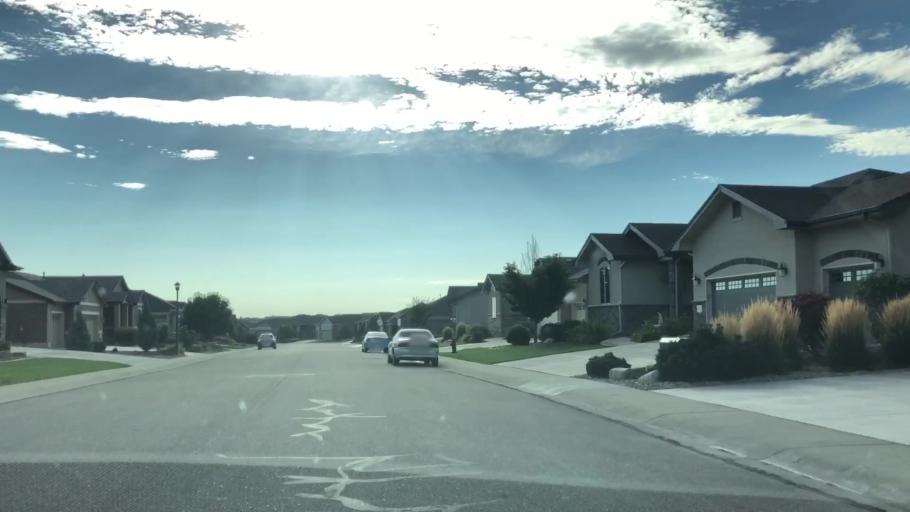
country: US
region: Colorado
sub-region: Weld County
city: Windsor
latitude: 40.4553
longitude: -104.9705
